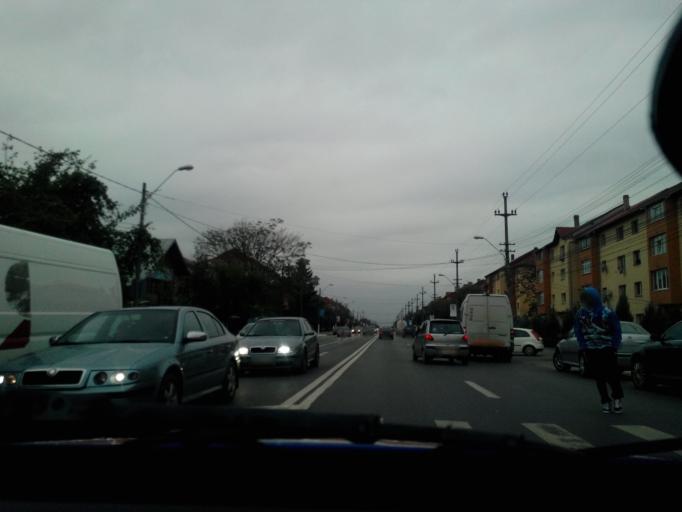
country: RO
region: Ilfov
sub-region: Comuna Bragadiru
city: Bragadiru
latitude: 44.3690
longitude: 25.9739
